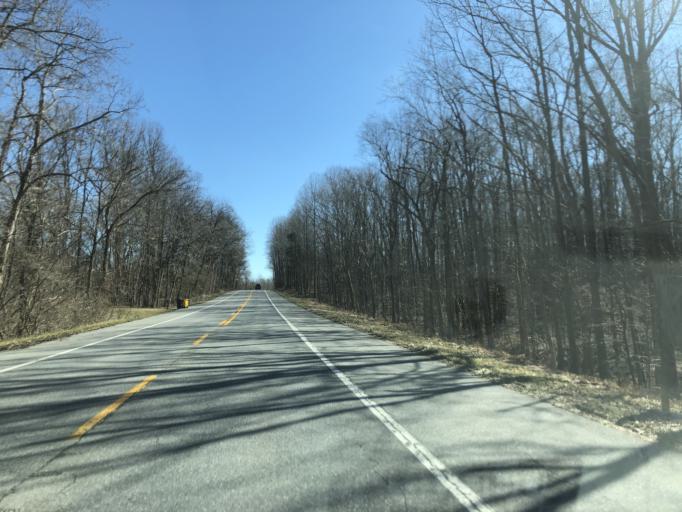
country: US
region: Maryland
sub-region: Calvert County
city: Dunkirk
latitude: 38.7913
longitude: -76.6598
